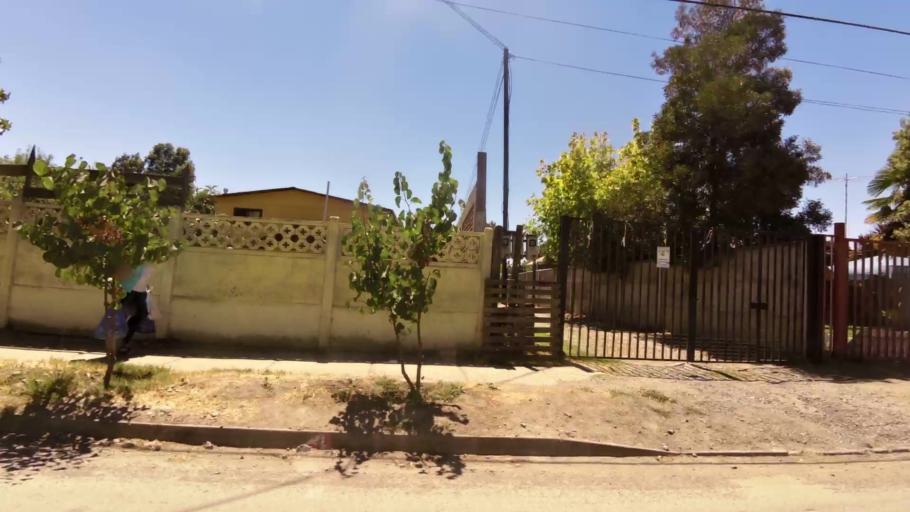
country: CL
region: O'Higgins
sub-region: Provincia de Cachapoal
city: Rancagua
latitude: -34.2267
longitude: -70.7882
